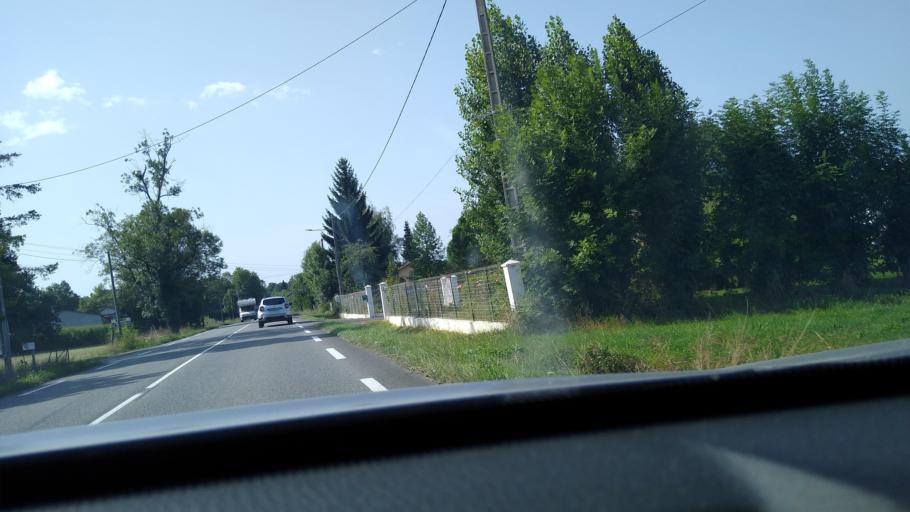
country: FR
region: Midi-Pyrenees
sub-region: Departement de la Haute-Garonne
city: Salies-du-Salat
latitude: 43.0599
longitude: 0.9749
